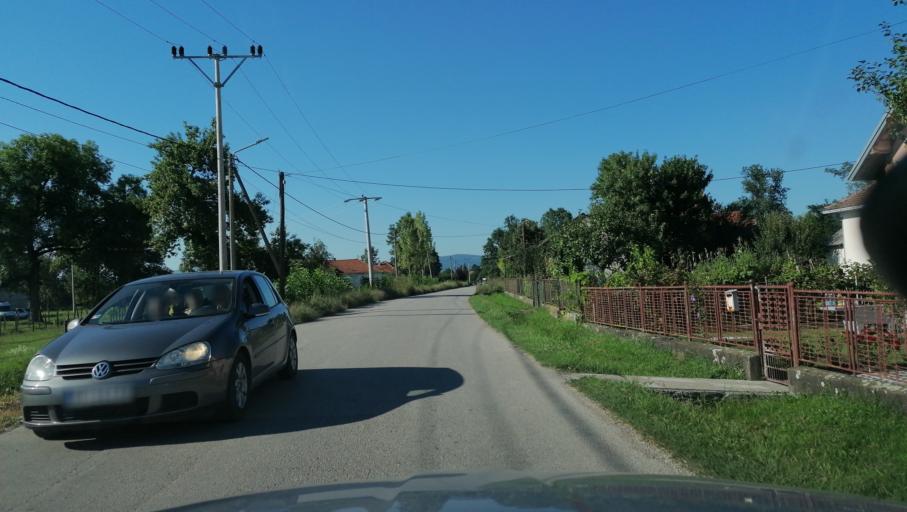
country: RS
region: Central Serbia
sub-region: Raski Okrug
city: Kraljevo
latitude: 43.8331
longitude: 20.5949
